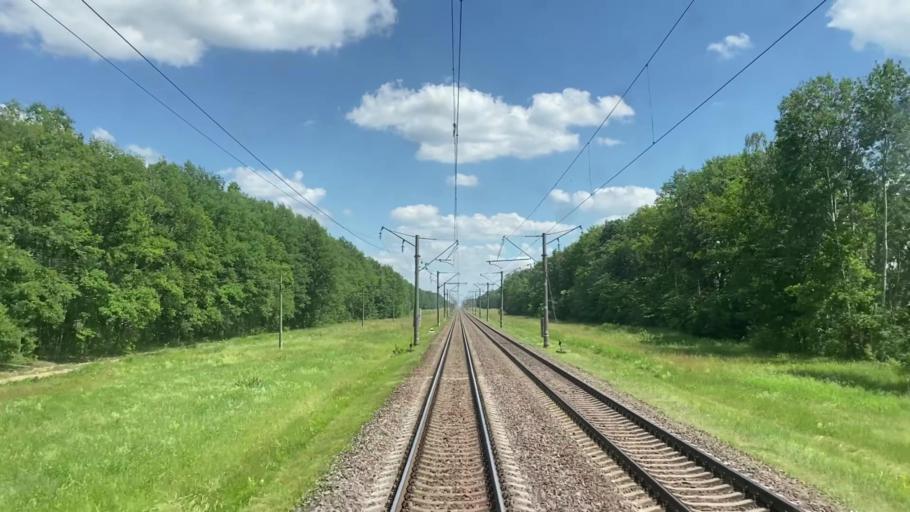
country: BY
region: Brest
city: Pruzhany
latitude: 52.5053
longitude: 24.6590
